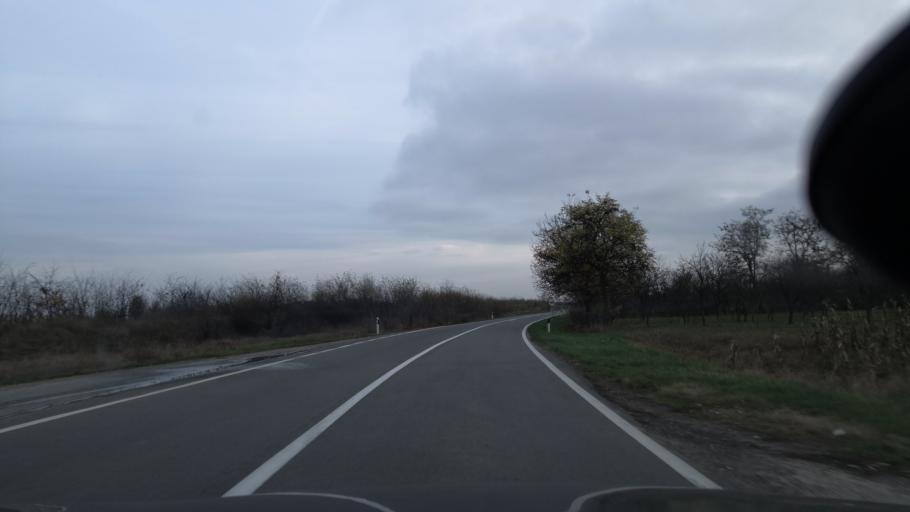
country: RS
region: Autonomna Pokrajina Vojvodina
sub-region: Severnobanatski Okrug
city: Coka
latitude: 45.9616
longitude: 20.1326
